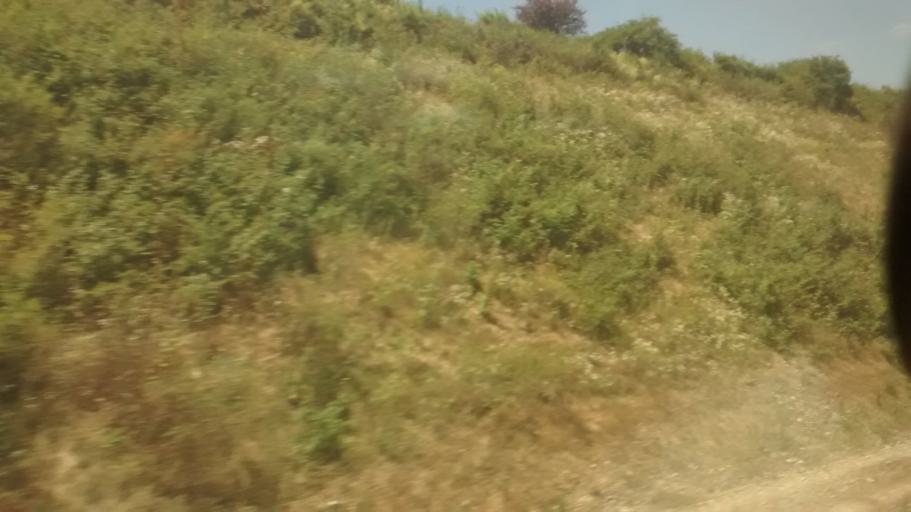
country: FR
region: Rhone-Alpes
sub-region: Departement du Rhone
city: Saint-Laurent-de-Mure
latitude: 45.7046
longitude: 5.0734
